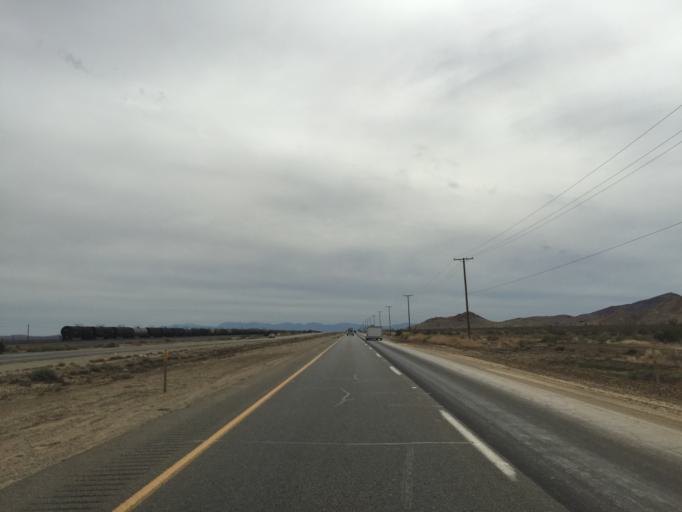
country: US
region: California
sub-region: Kern County
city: Mojave
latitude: 35.0222
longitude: -118.1651
